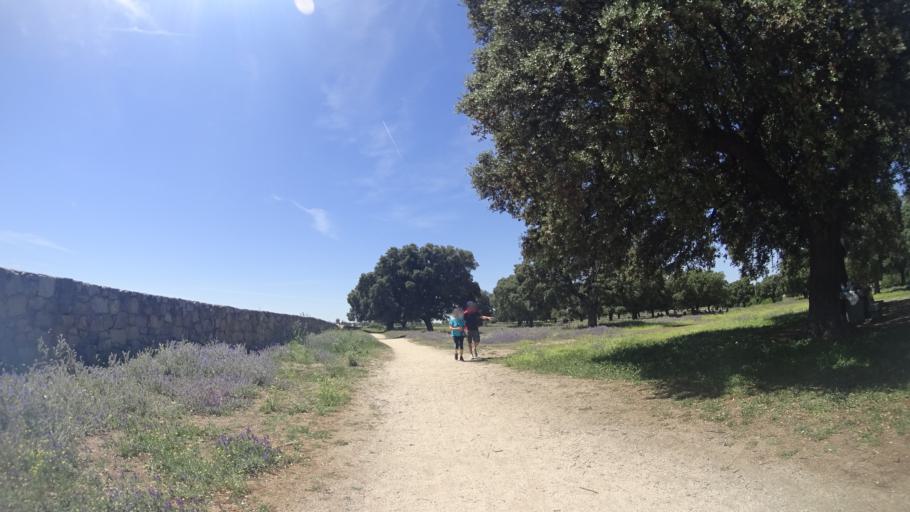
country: ES
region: Madrid
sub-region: Provincia de Madrid
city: Collado-Villalba
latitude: 40.6502
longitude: -4.0037
